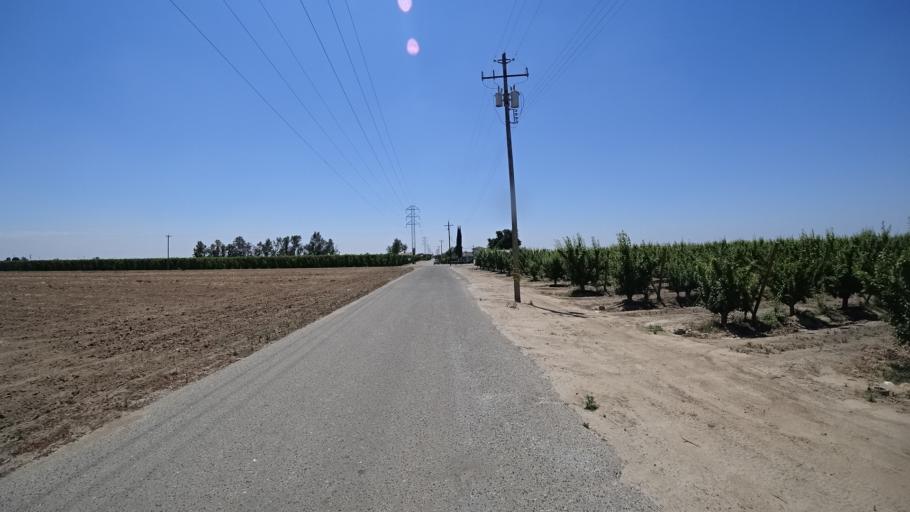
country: US
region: California
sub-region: Fresno County
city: Kingsburg
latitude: 36.4750
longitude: -119.5912
